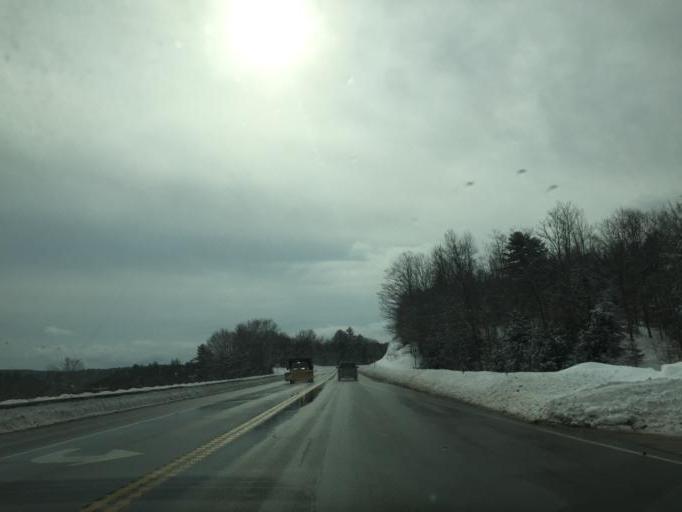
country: US
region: New Hampshire
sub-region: Carroll County
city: Sanbornville
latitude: 43.5293
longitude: -71.0273
